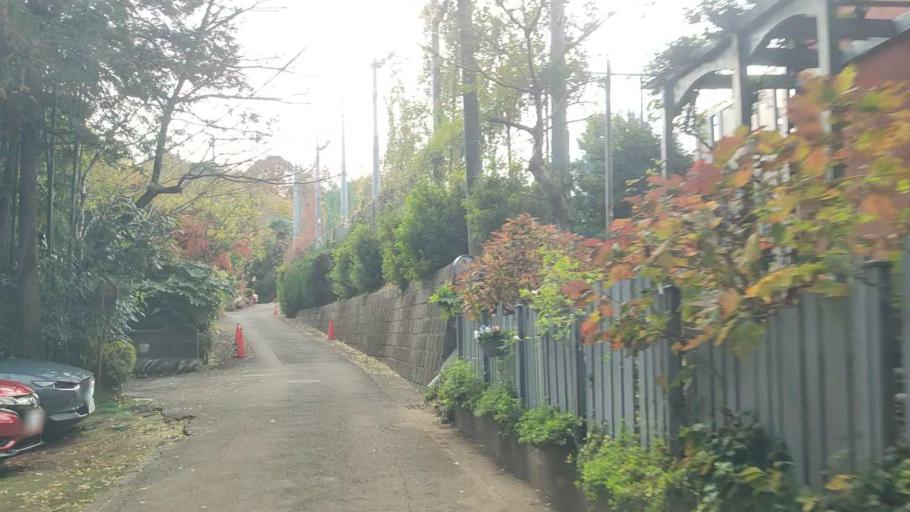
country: JP
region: Kanagawa
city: Minami-rinkan
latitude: 35.4950
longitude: 139.4964
